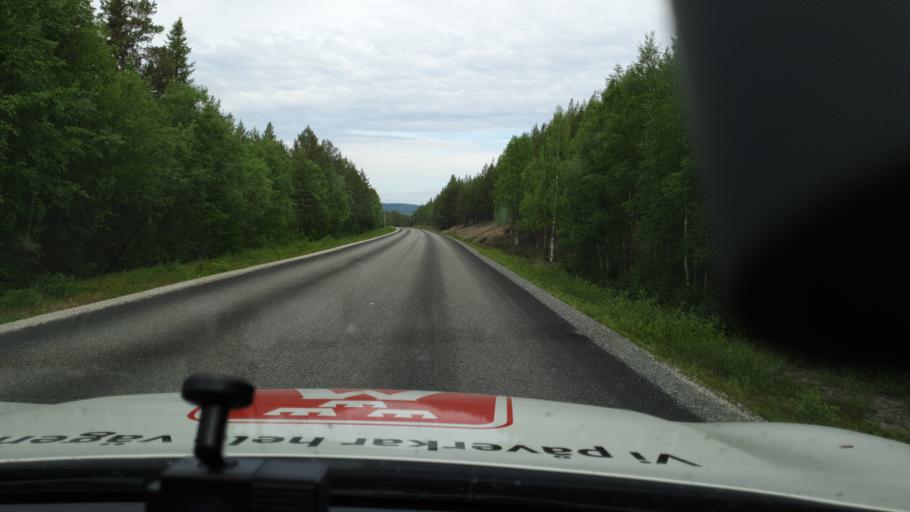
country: SE
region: Vaesterbotten
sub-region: Mala Kommun
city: Mala
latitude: 64.9158
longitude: 18.6439
